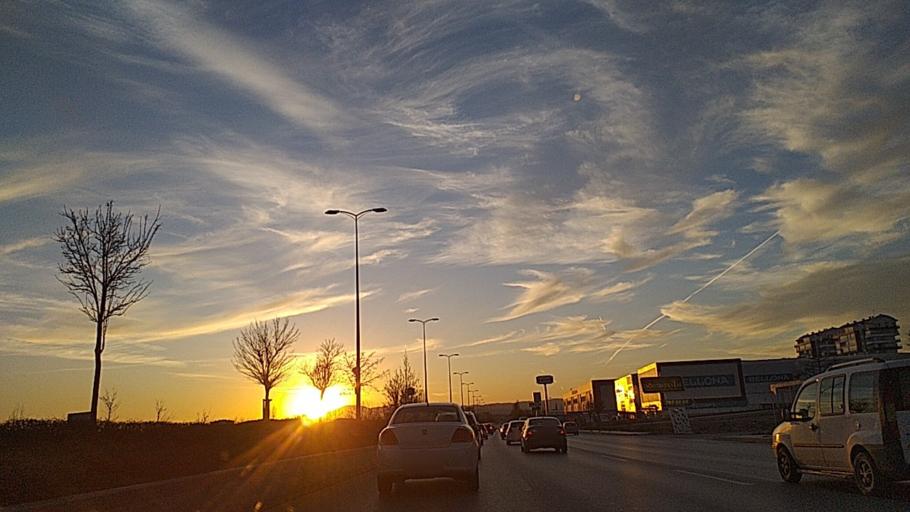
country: TR
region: Ankara
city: Etimesgut
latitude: 39.9629
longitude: 32.6571
